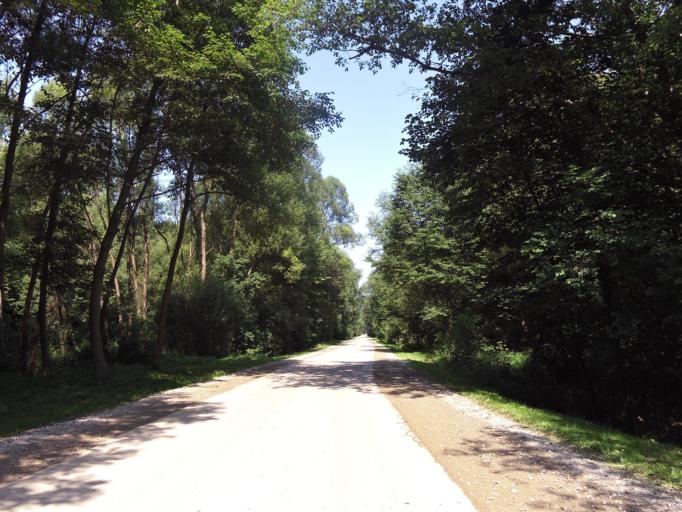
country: PL
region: Silesian Voivodeship
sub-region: Powiat zywiecki
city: Cisiec
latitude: 49.5942
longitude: 19.0984
